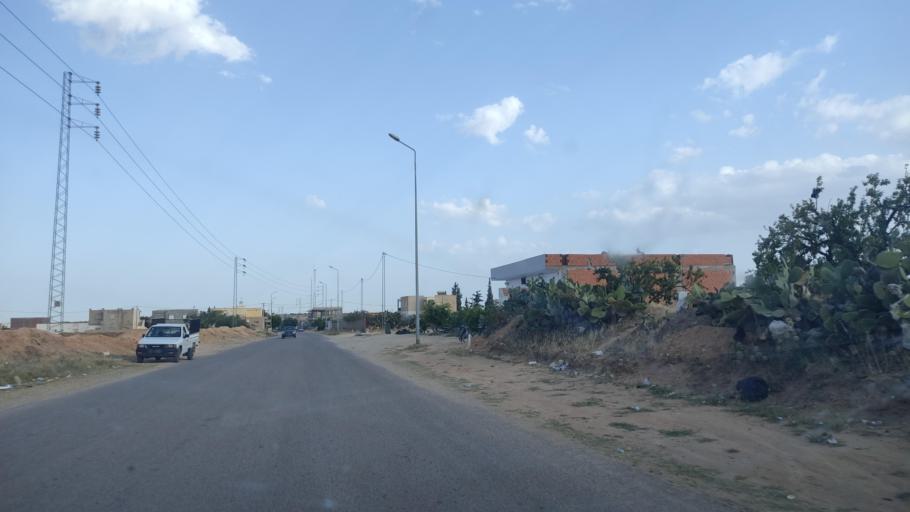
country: TN
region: Safaqis
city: Sfax
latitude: 34.8478
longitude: 10.6142
